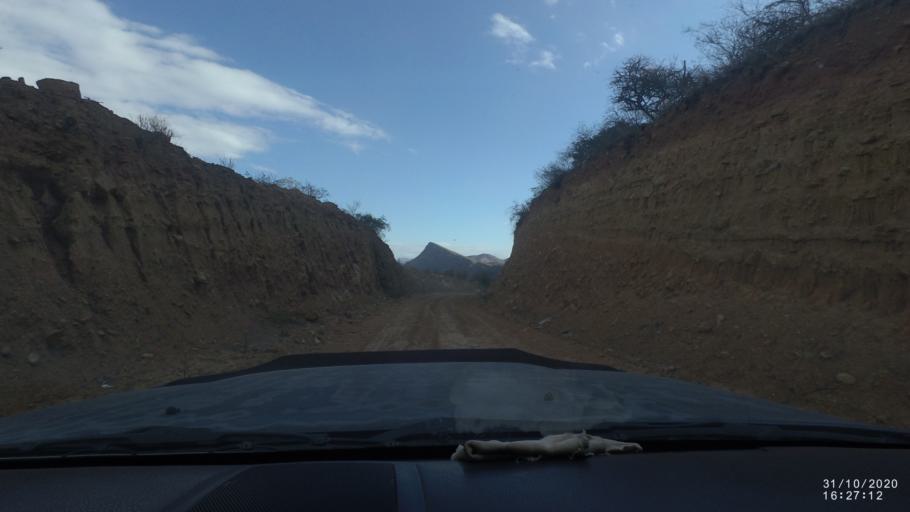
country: BO
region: Chuquisaca
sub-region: Provincia Zudanez
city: Mojocoya
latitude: -18.4047
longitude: -64.5855
